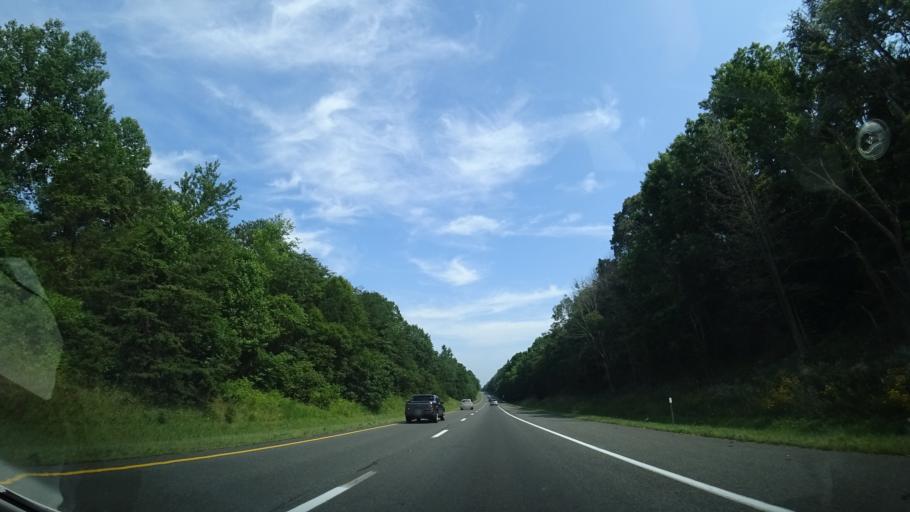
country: US
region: Virginia
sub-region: Goochland County
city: Goochland
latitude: 37.8394
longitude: -77.9770
